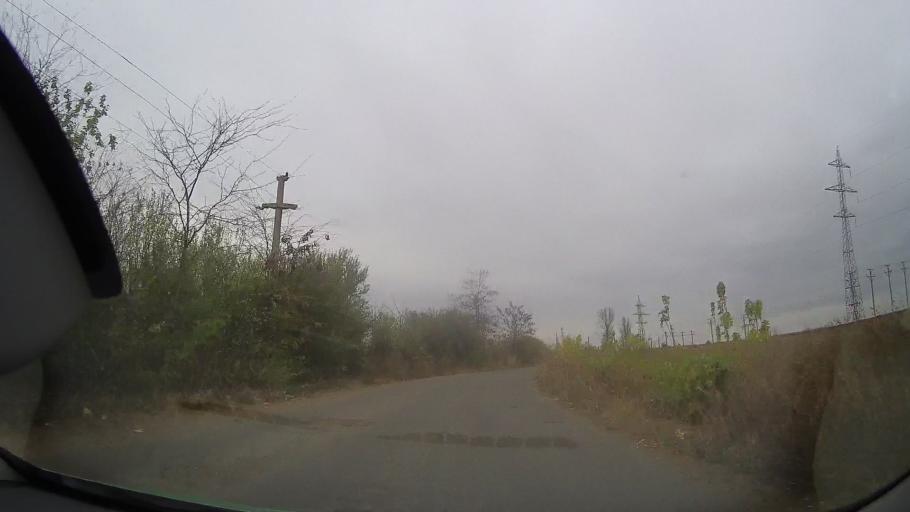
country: RO
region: Braila
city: Dudesti
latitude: 44.8961
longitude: 27.4335
